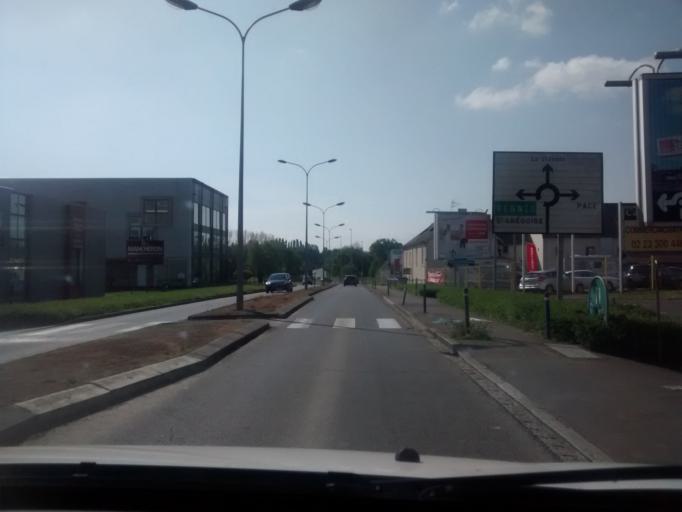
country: FR
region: Brittany
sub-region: Departement d'Ille-et-Vilaine
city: Montgermont
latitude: 48.1543
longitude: -1.7073
